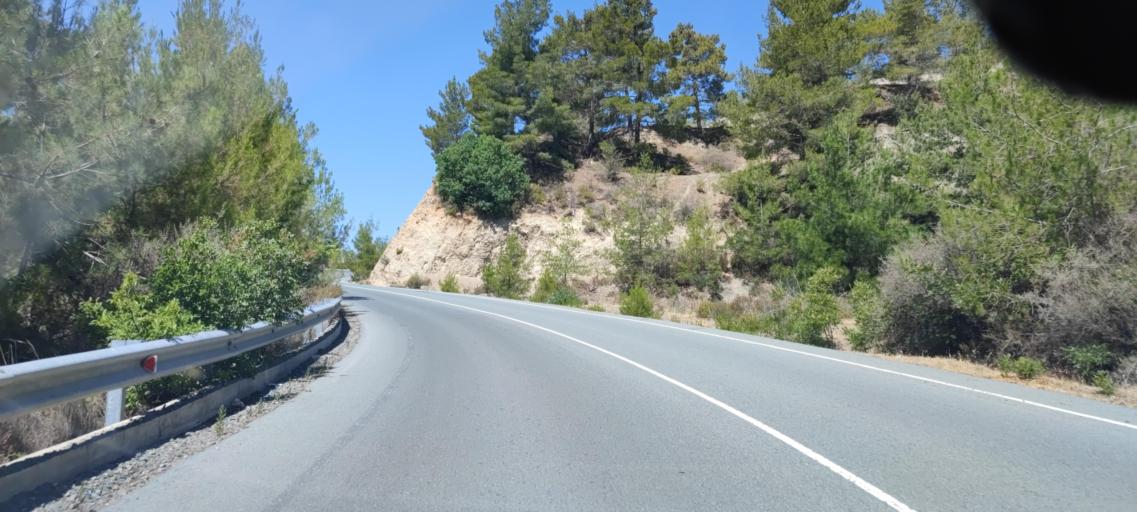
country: CY
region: Limassol
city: Pachna
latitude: 34.8994
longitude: 32.8177
